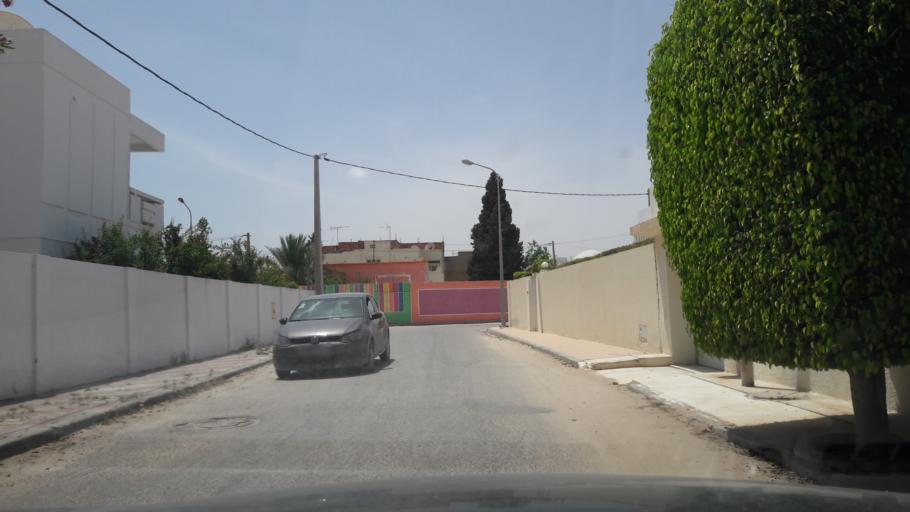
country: TN
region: Safaqis
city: Sfax
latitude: 34.7768
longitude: 10.7535
